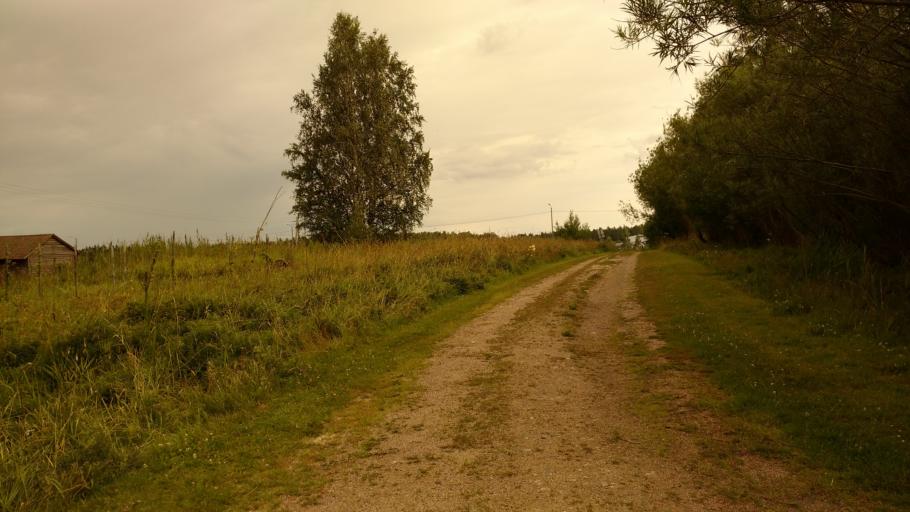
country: FI
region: Varsinais-Suomi
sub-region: Turku
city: Piikkioe
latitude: 60.4323
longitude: 22.4673
